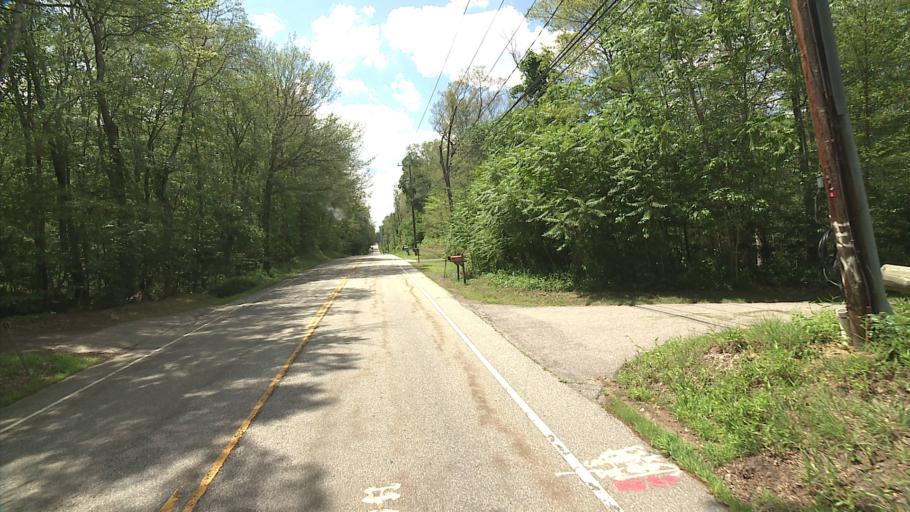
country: US
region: Connecticut
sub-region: Middlesex County
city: Higganum
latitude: 41.5216
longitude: -72.5122
